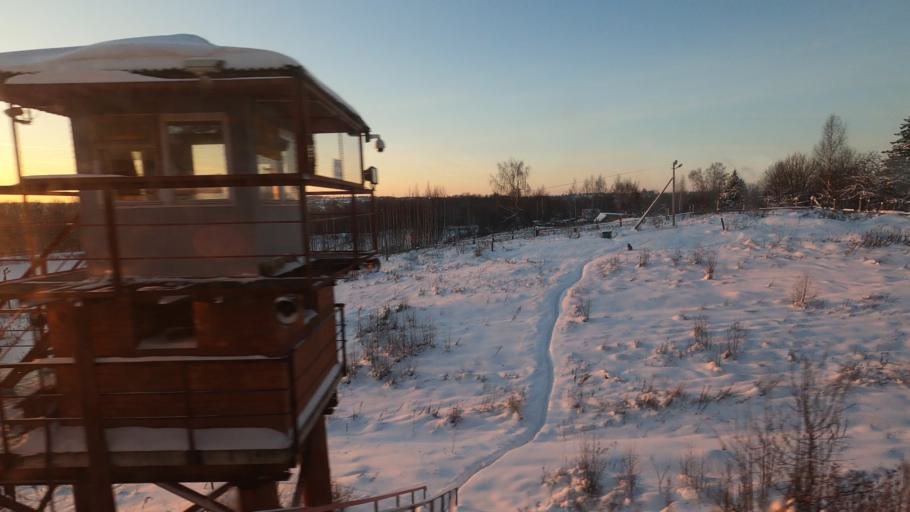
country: RU
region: Moskovskaya
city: Dedenevo
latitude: 56.2615
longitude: 37.5113
